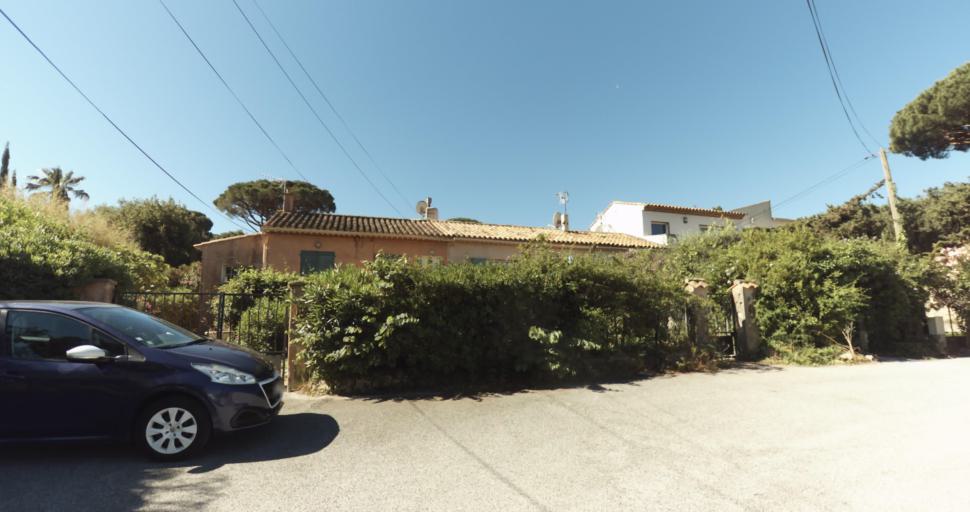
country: FR
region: Provence-Alpes-Cote d'Azur
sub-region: Departement du Var
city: Saint-Tropez
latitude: 43.2625
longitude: 6.6135
